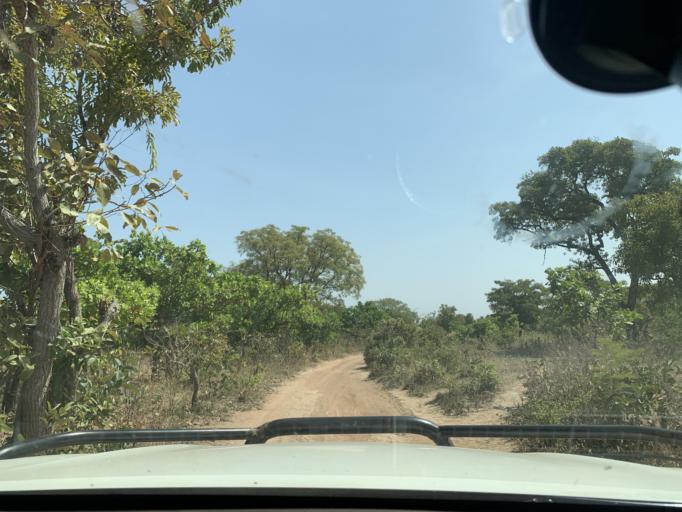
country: ML
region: Sikasso
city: Kolondieba
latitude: 10.8381
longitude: -6.7970
